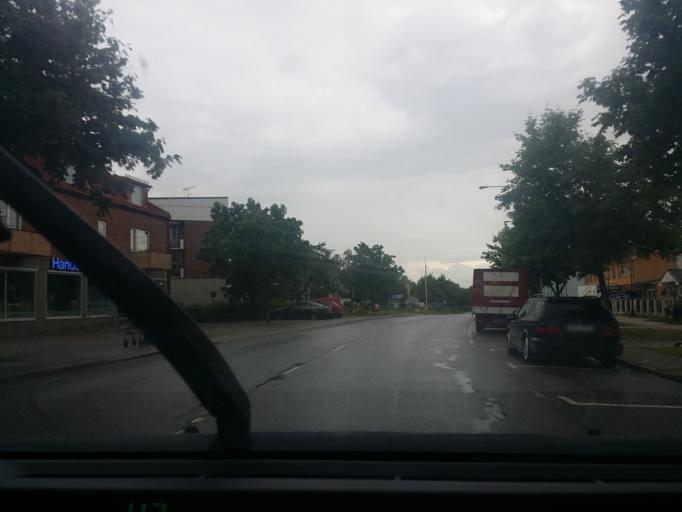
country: SE
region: OErebro
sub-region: Lindesbergs Kommun
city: Frovi
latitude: 59.4664
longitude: 15.3618
